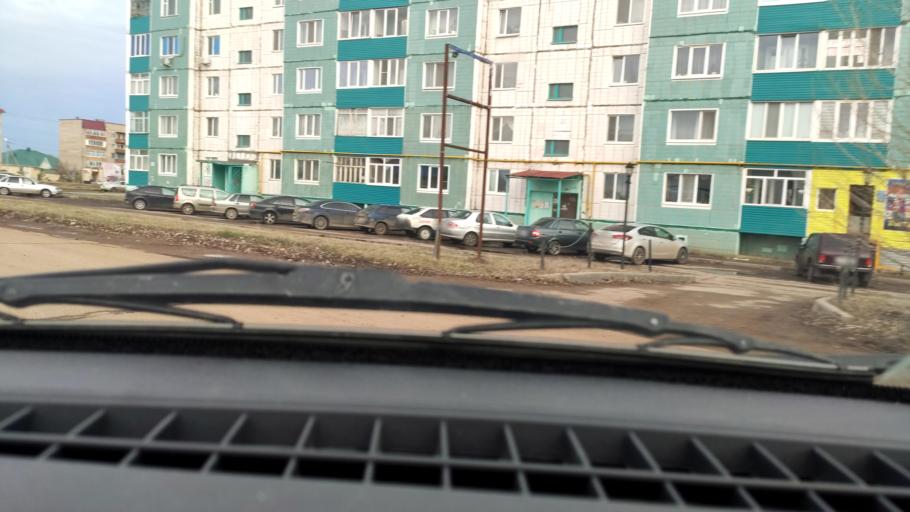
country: RU
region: Bashkortostan
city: Davlekanovo
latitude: 54.2283
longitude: 55.0323
